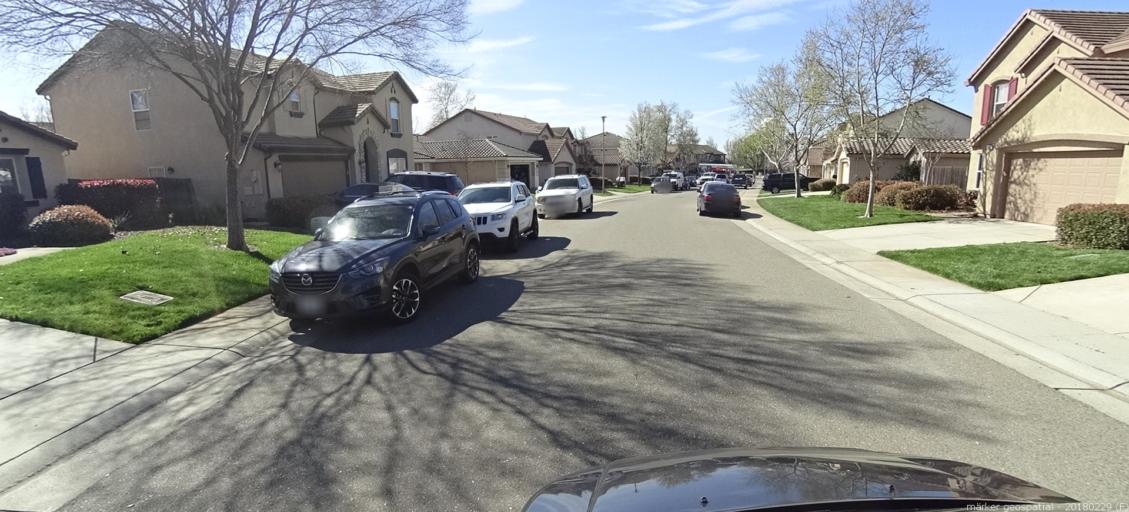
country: US
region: California
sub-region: Sacramento County
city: Rancho Cordova
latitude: 38.5477
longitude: -121.2780
